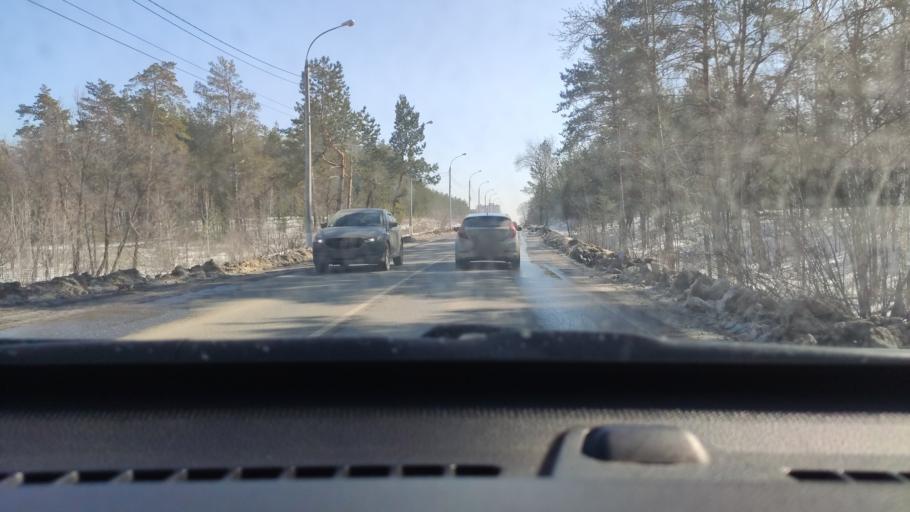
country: RU
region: Samara
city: Zhigulevsk
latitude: 53.4775
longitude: 49.4340
